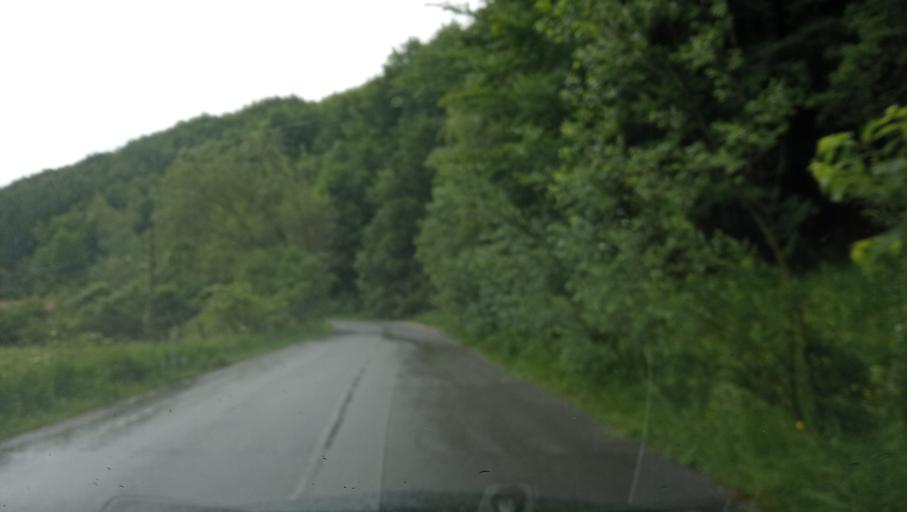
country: RO
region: Hunedoara
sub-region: Oras Petrila
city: Petrila
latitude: 45.3957
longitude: 23.4374
